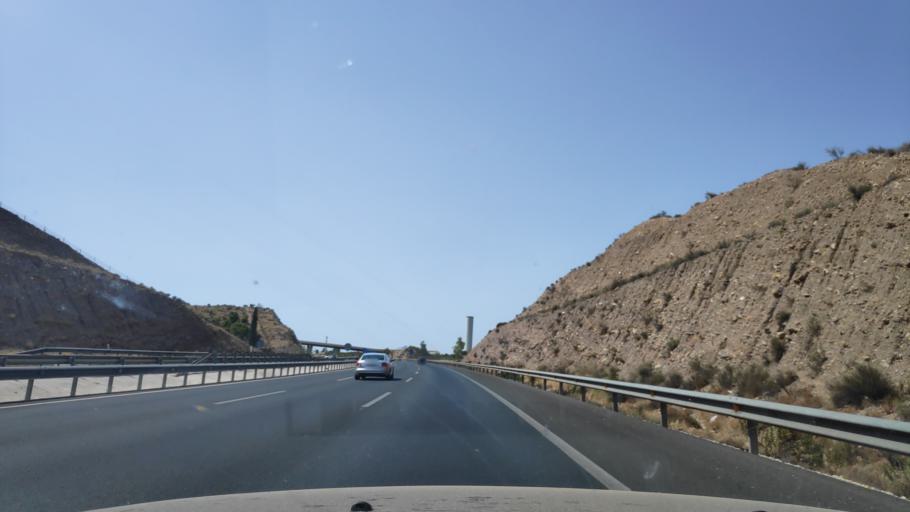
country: ES
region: Murcia
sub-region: Murcia
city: Molina de Segura
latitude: 38.0423
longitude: -1.1627
